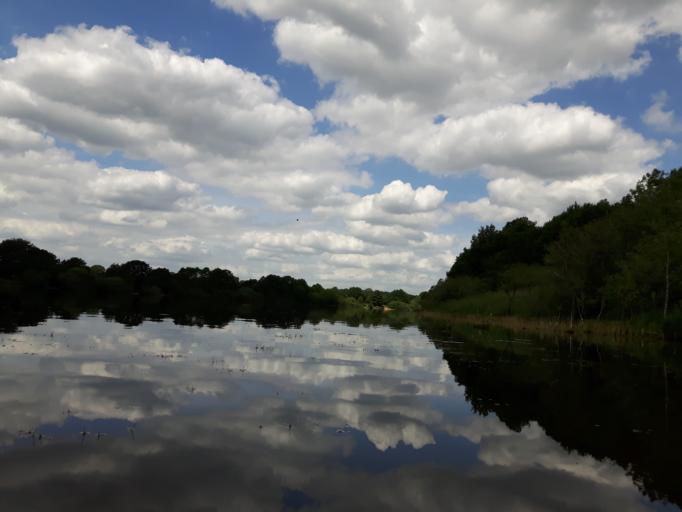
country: DE
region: Schleswig-Holstein
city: Muhbrook
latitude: 54.1504
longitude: 10.0106
